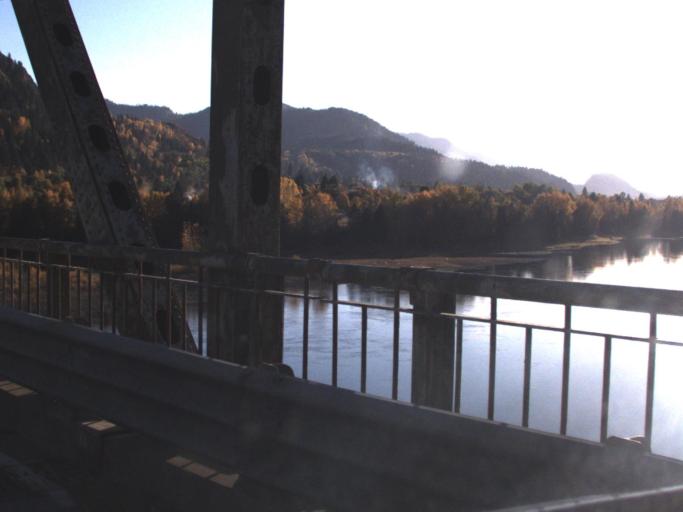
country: CA
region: British Columbia
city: Rossland
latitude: 48.9232
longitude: -117.7770
